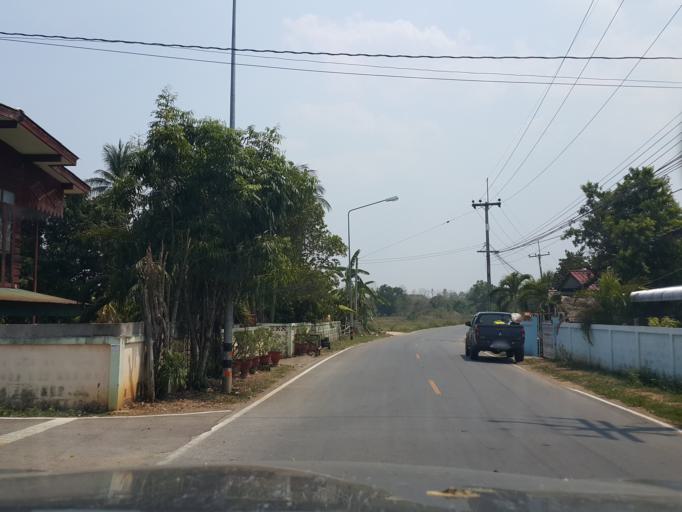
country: TH
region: Lampang
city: Mae Phrik
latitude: 17.4978
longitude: 99.1277
